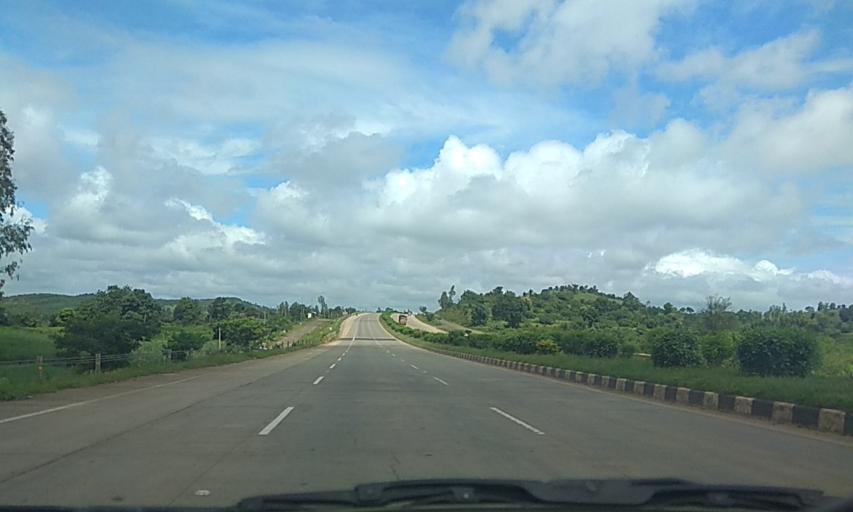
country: IN
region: Karnataka
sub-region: Dharwad
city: Alnavar
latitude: 15.6121
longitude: 74.7656
